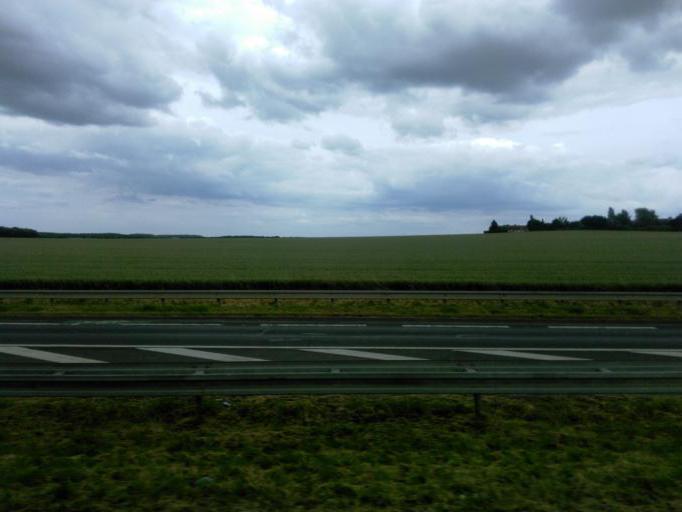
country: FR
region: Ile-de-France
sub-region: Departement du Val-d'Oise
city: Osny
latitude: 49.0888
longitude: 2.0601
